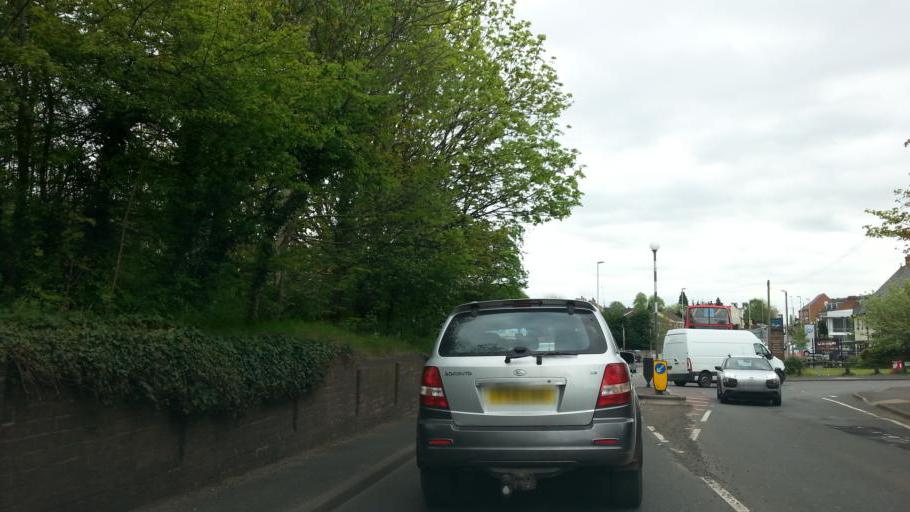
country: GB
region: England
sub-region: Dudley
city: Stourbridge
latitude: 52.4746
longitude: -2.1563
